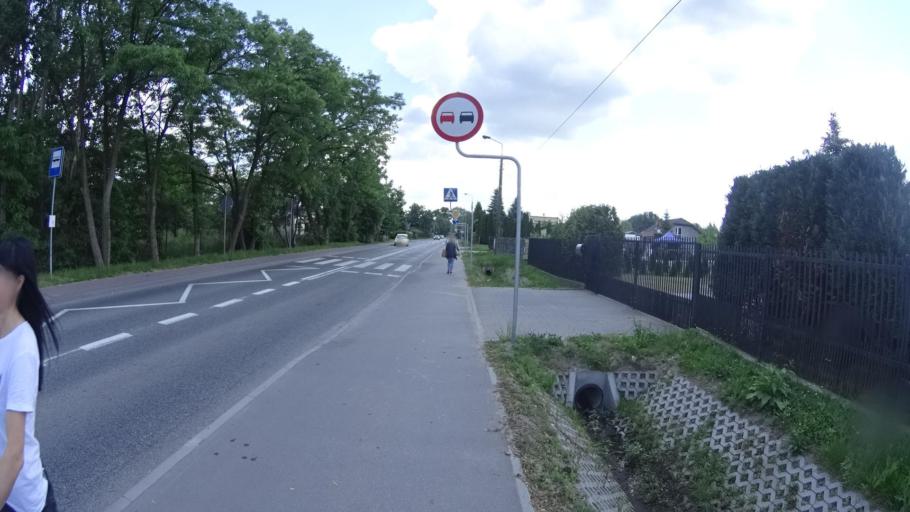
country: PL
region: Masovian Voivodeship
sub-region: Powiat pruszkowski
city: Nadarzyn
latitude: 52.0987
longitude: 20.8059
